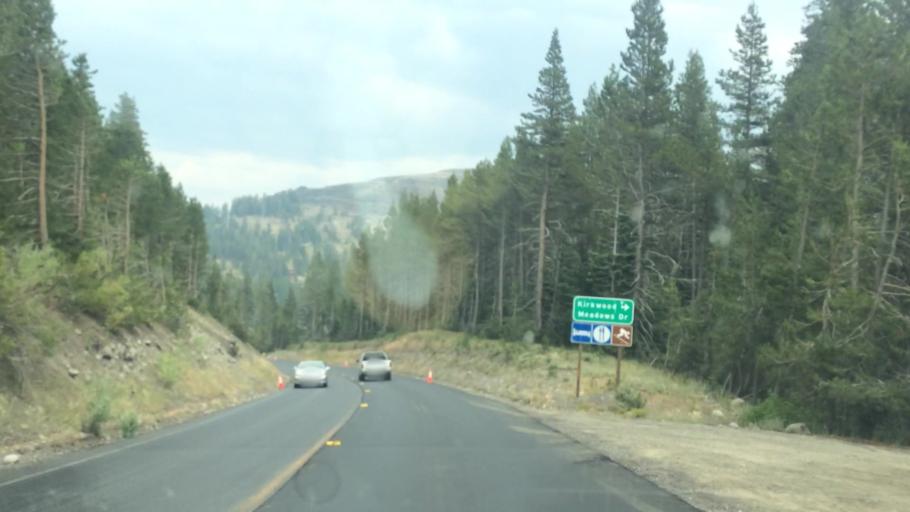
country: US
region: California
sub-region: El Dorado County
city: South Lake Tahoe
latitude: 38.7000
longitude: -120.0816
